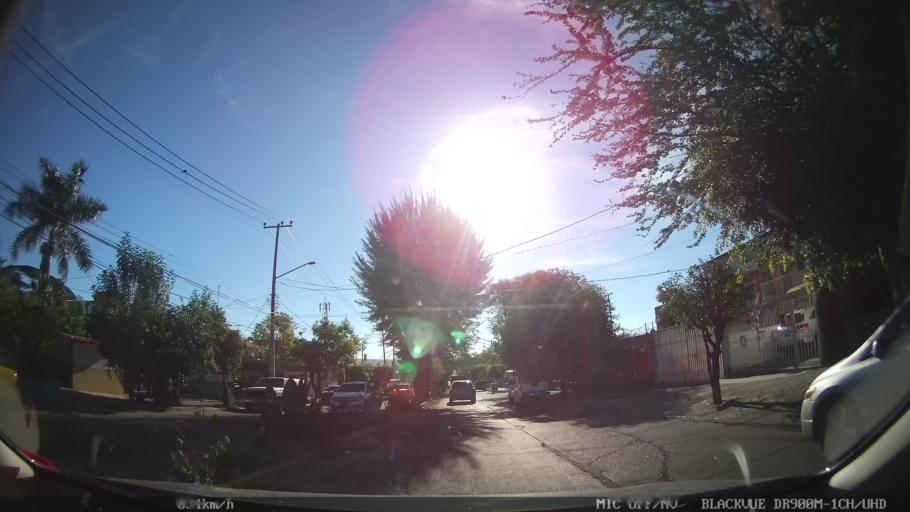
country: MX
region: Jalisco
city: Tlaquepaque
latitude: 20.7010
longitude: -103.2879
